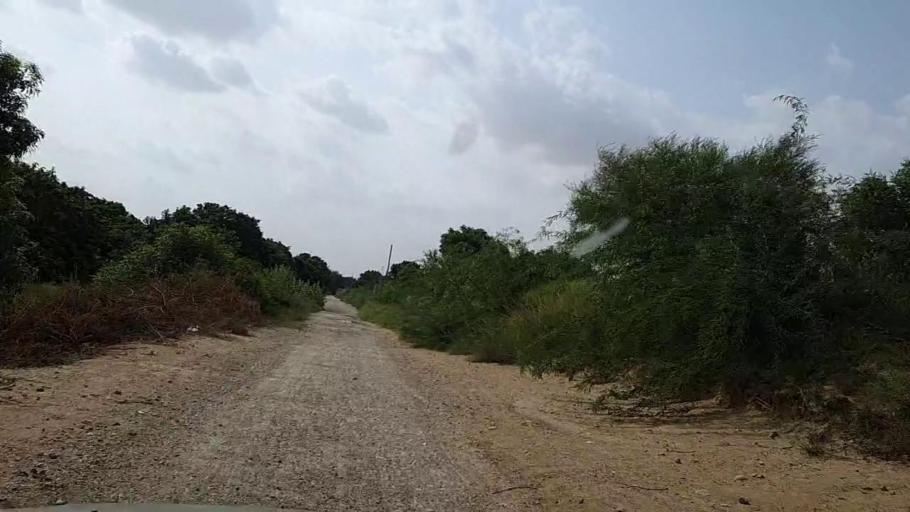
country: PK
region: Sindh
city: Kotri
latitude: 25.2401
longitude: 68.2660
